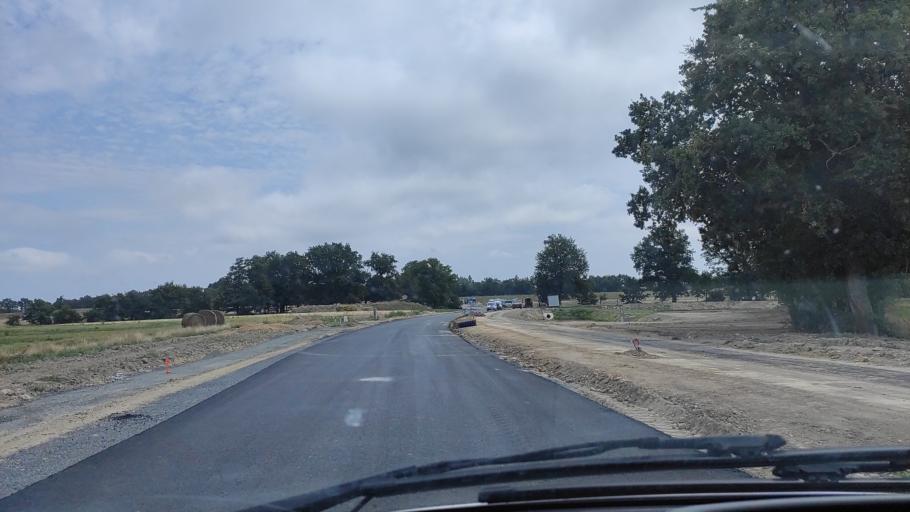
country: FR
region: Pays de la Loire
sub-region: Departement de la Vendee
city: Dompierre-sur-Yon
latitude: 46.7402
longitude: -1.4217
